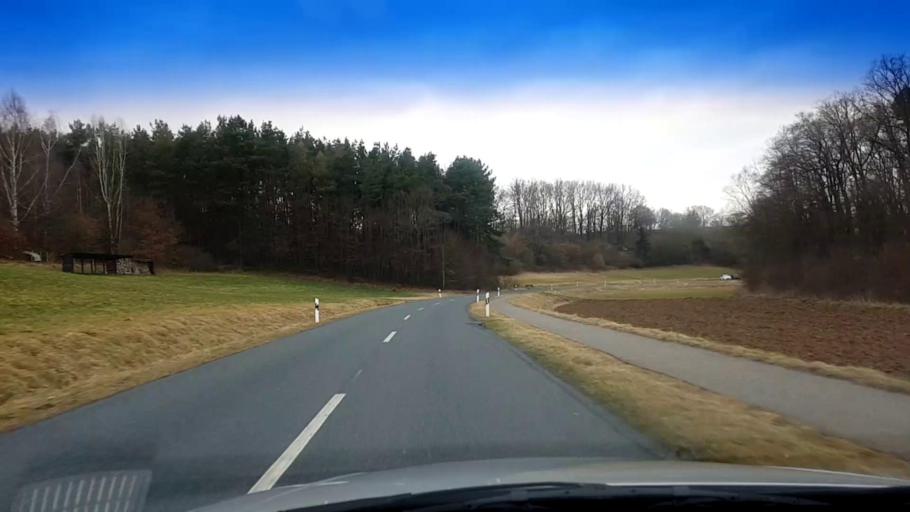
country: DE
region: Bavaria
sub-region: Upper Franconia
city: Bischberg
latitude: 49.9047
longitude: 10.8152
